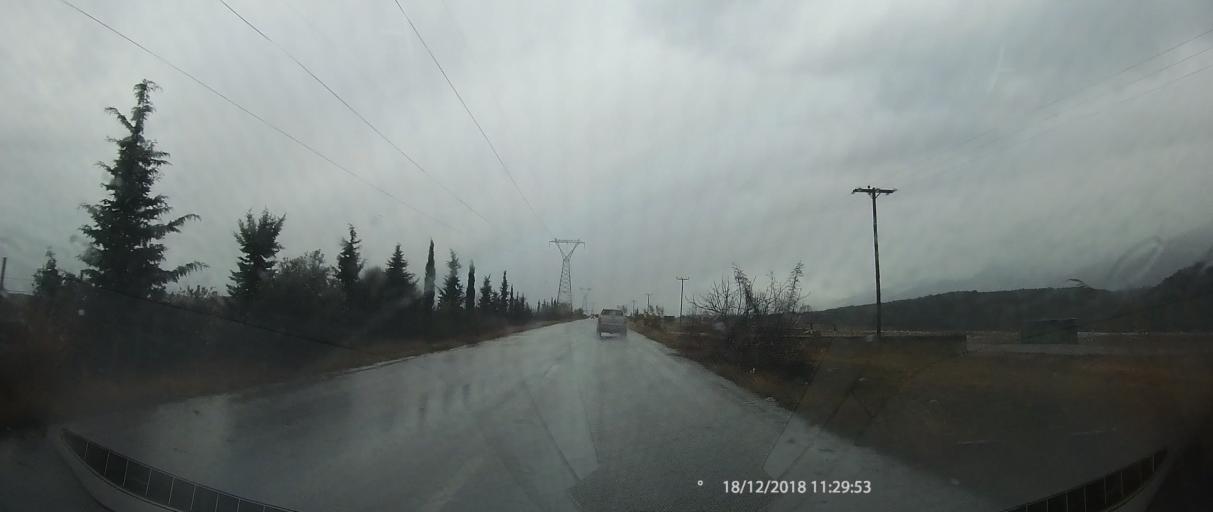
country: GR
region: Central Macedonia
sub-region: Nomos Pierias
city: Litochoro
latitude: 40.1299
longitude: 22.5221
